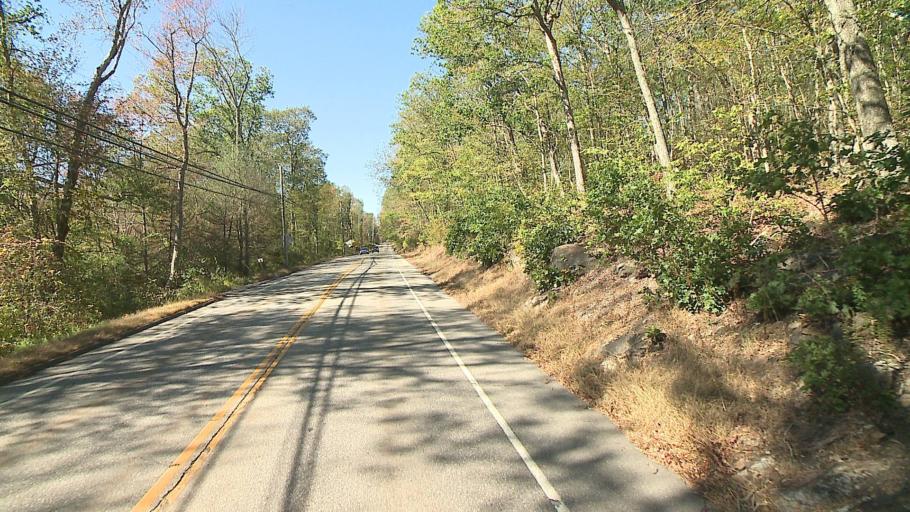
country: US
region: Connecticut
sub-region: Tolland County
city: Hebron
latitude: 41.6472
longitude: -72.4042
